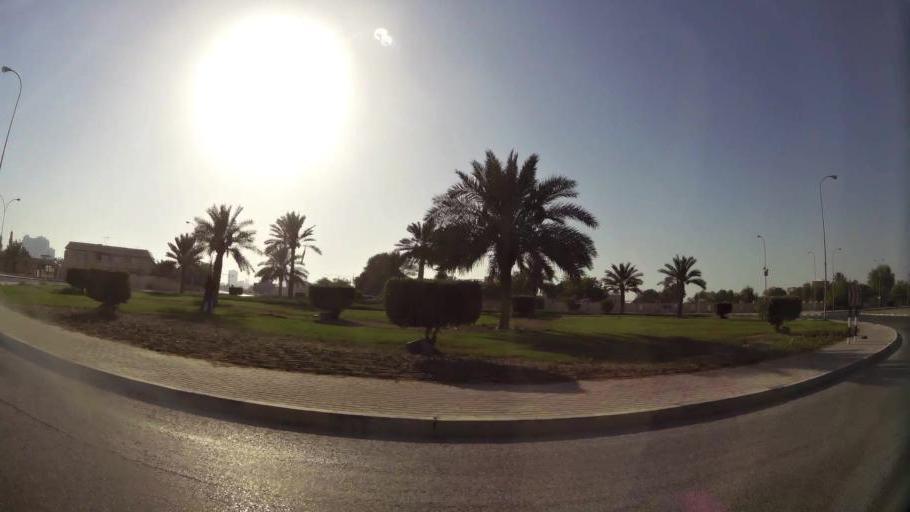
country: AE
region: Ajman
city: Ajman
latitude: 25.4085
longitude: 55.4660
